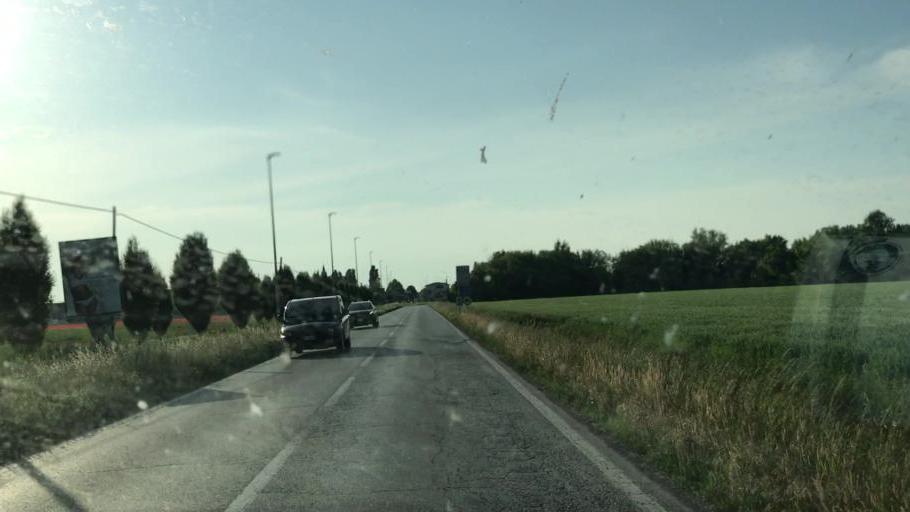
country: IT
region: Lombardy
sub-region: Provincia di Mantova
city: Casaloldo
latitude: 45.2492
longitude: 10.4889
